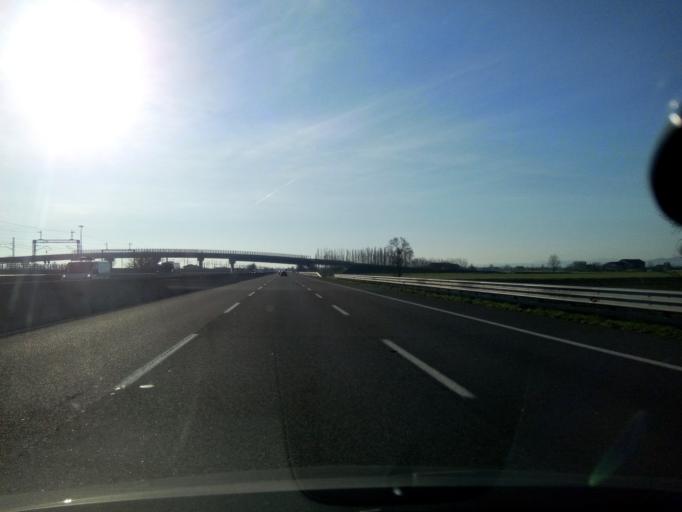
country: IT
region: Emilia-Romagna
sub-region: Provincia di Reggio Emilia
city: Campegine
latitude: 44.7584
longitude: 10.5400
